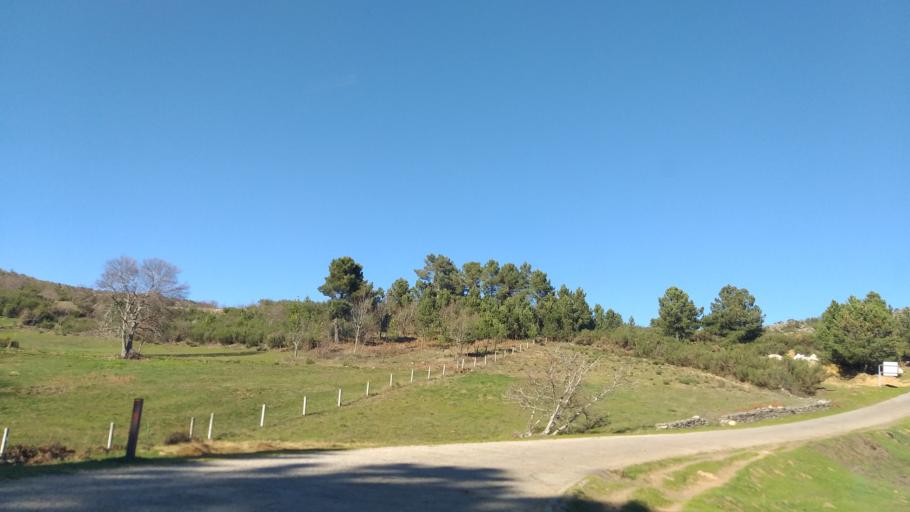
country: PT
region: Guarda
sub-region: Celorico da Beira
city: Celorico da Beira
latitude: 40.5219
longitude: -7.3936
